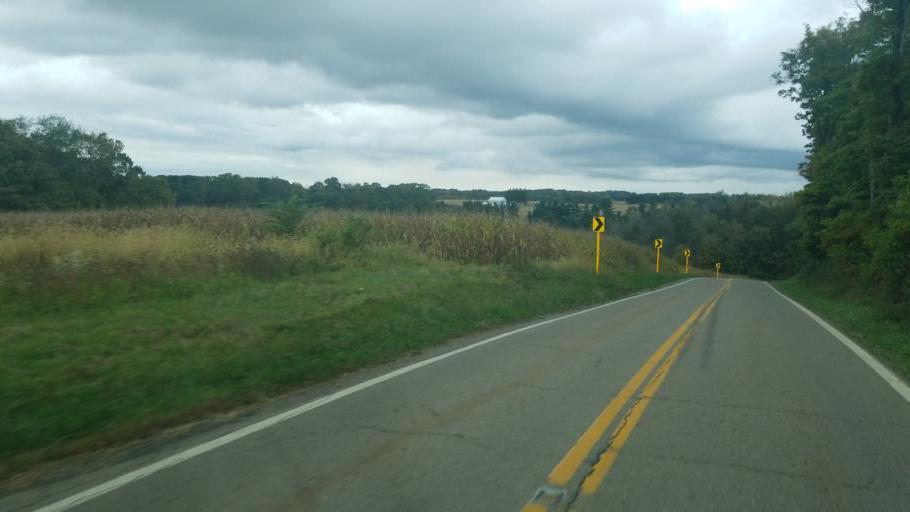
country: US
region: Ohio
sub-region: Ashland County
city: Loudonville
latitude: 40.5373
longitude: -82.1575
